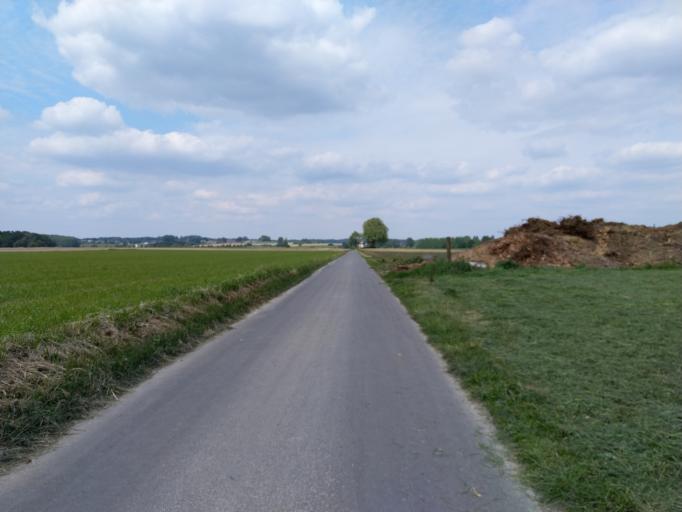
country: BE
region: Wallonia
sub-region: Province du Hainaut
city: Lens
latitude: 50.5911
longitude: 3.9481
